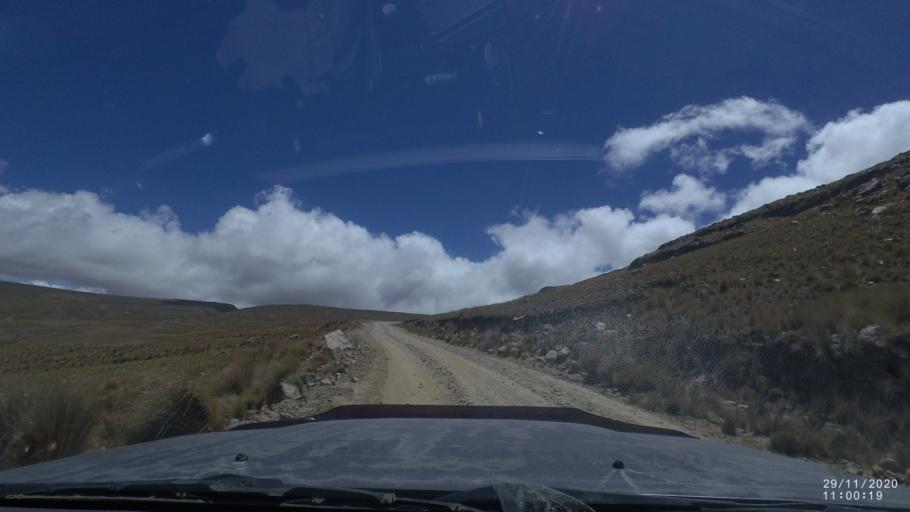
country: BO
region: Cochabamba
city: Cochabamba
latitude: -17.2046
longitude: -66.2268
